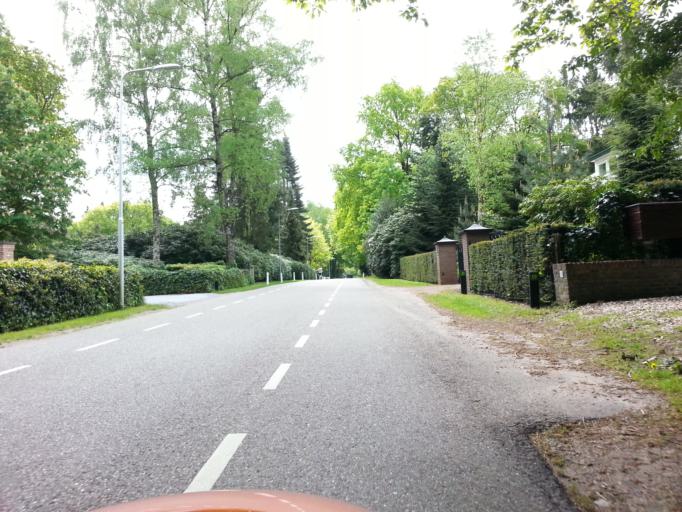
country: NL
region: Gelderland
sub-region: Gemeente Ede
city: Ede
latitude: 52.0687
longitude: 5.6862
